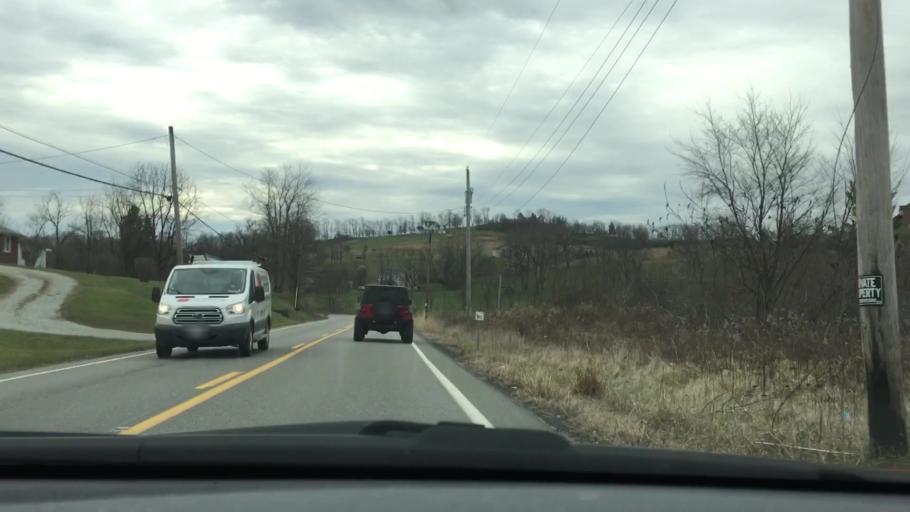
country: US
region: Pennsylvania
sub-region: Washington County
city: Muse
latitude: 40.2865
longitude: -80.2128
